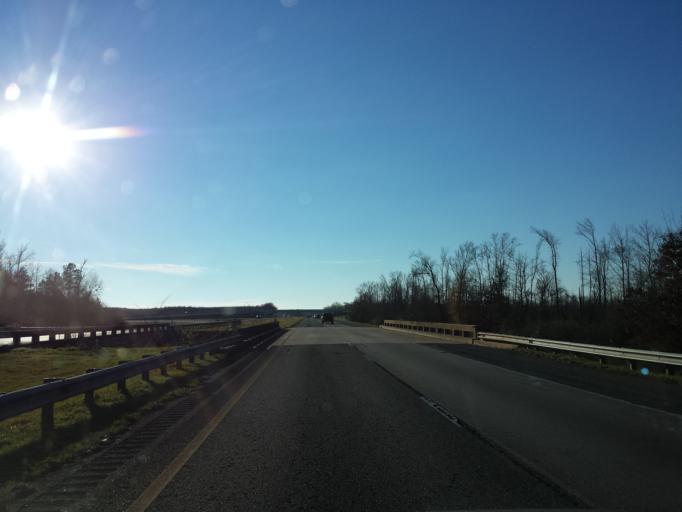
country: US
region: Alabama
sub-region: Tuscaloosa County
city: Tuscaloosa
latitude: 33.1551
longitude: -87.5906
